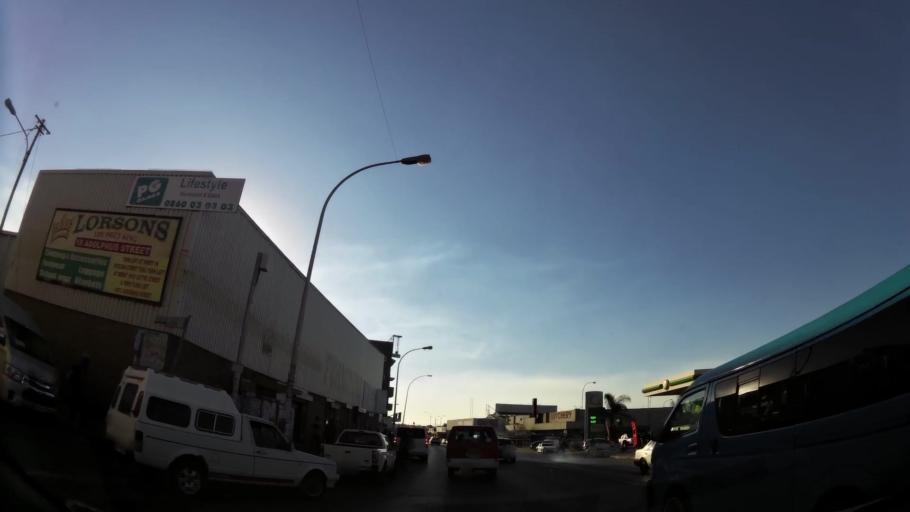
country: ZA
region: Gauteng
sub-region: City of Johannesburg Metropolitan Municipality
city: Roodepoort
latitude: -26.1611
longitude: 27.8697
